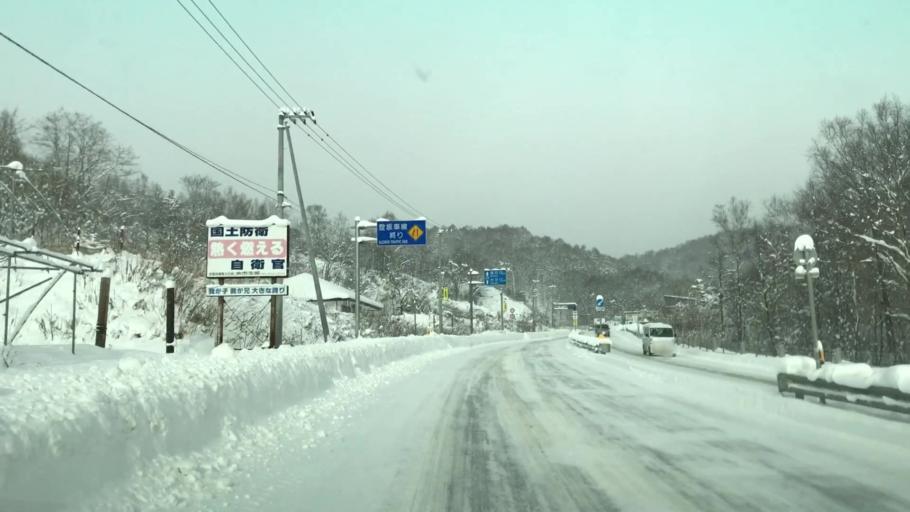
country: JP
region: Hokkaido
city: Yoichi
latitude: 43.2170
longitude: 140.7428
